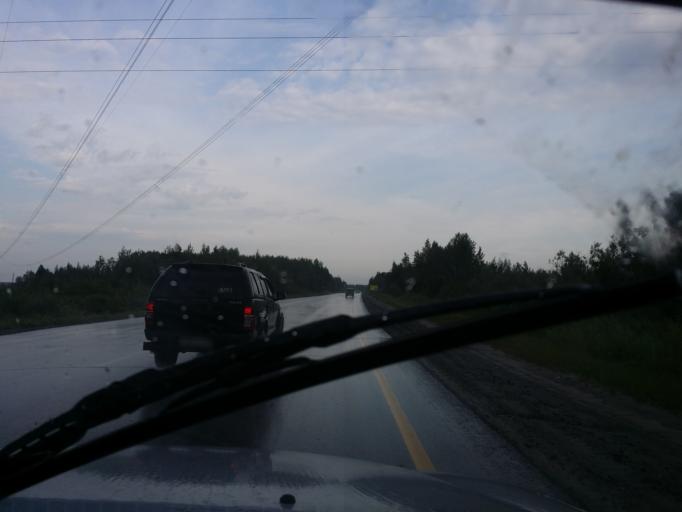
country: RU
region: Khanty-Mansiyskiy Avtonomnyy Okrug
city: Megion
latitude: 61.1029
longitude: 76.0489
